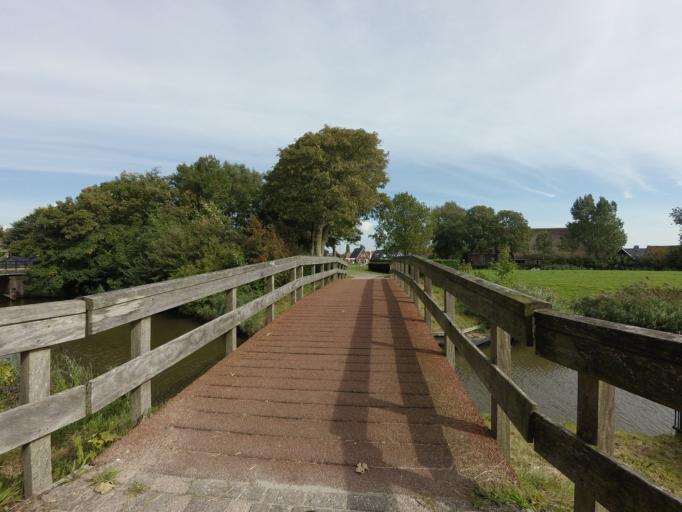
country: NL
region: Friesland
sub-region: Gemeente Franekeradeel
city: Franeker
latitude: 53.1659
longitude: 5.5131
